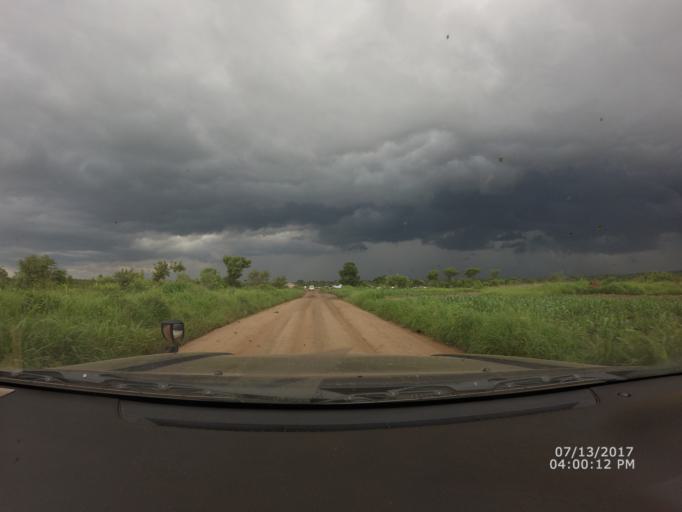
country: UG
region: Northern Region
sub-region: Yumbe District
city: Yumbe
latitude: 3.2960
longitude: 31.2883
